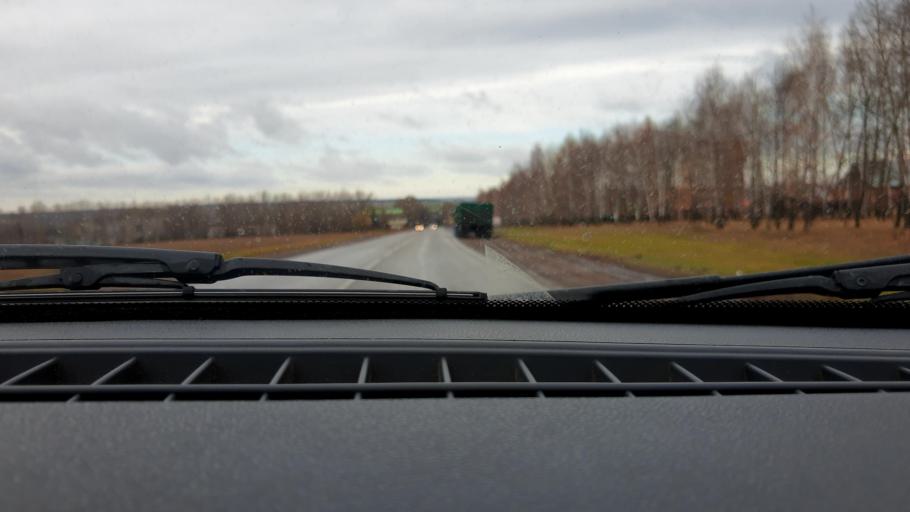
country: RU
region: Bashkortostan
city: Avdon
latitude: 54.8199
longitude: 55.7075
